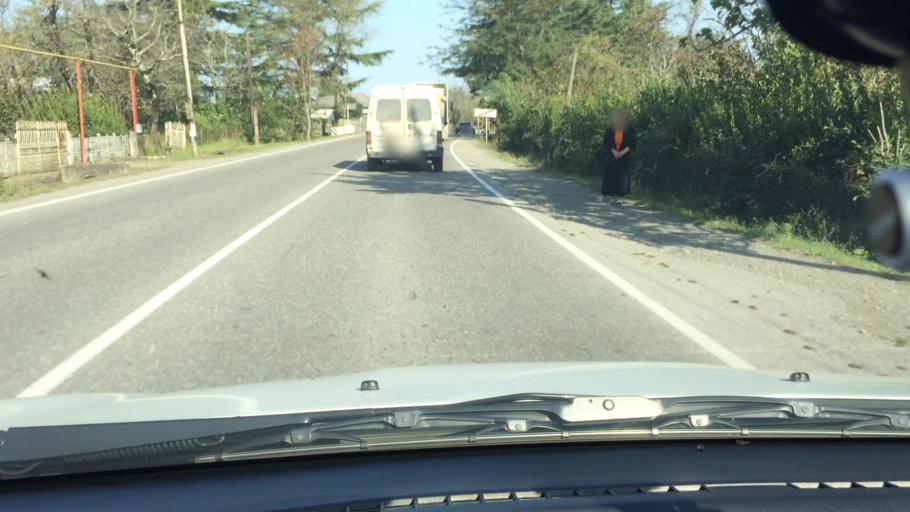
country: GE
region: Guria
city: Lanchkhuti
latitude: 42.0786
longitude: 42.0510
